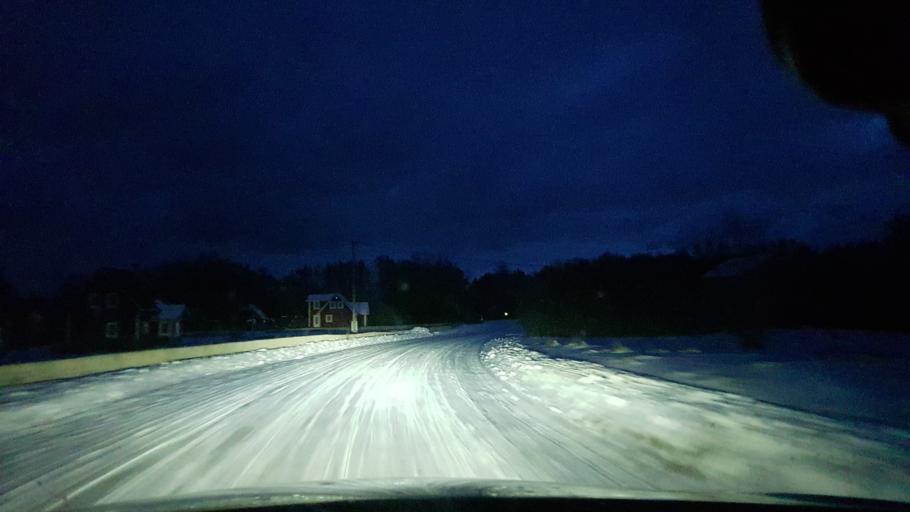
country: EE
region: Laeaene
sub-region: Haapsalu linn
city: Haapsalu
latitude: 59.2186
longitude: 23.5304
